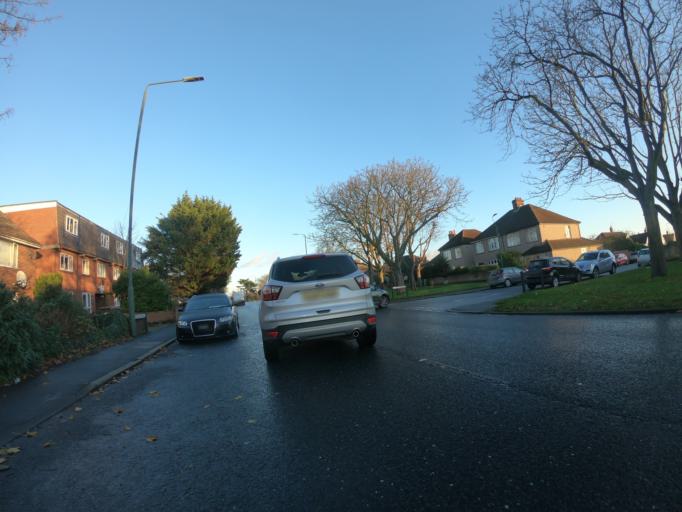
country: GB
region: England
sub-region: Greater London
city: Belvedere
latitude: 51.4838
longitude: 0.1401
